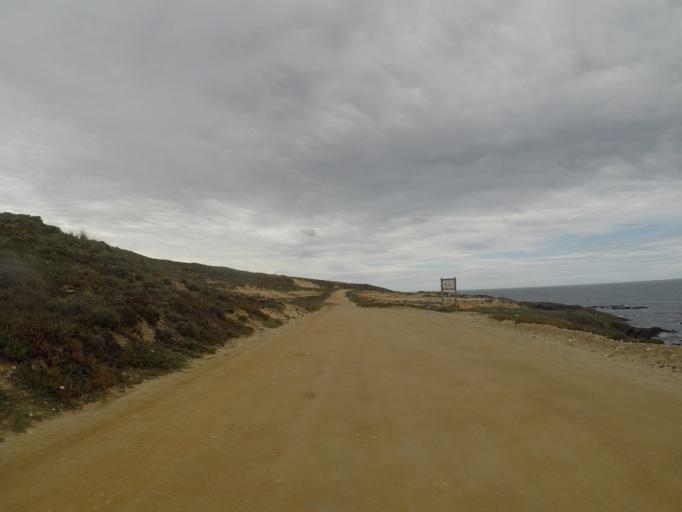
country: PT
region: Beja
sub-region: Odemira
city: Vila Nova de Milfontes
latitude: 37.6451
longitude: -8.8058
